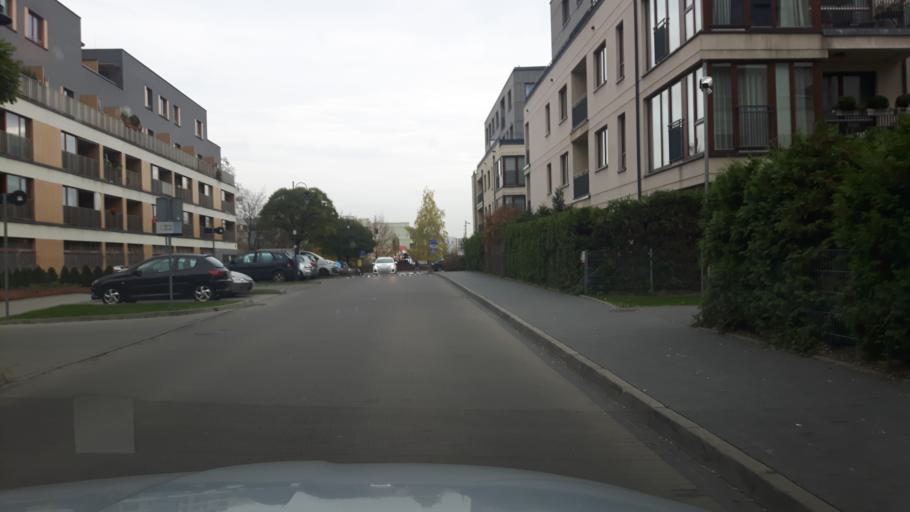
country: PL
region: Masovian Voivodeship
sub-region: Warszawa
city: Ursynow
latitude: 52.1597
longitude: 21.0670
